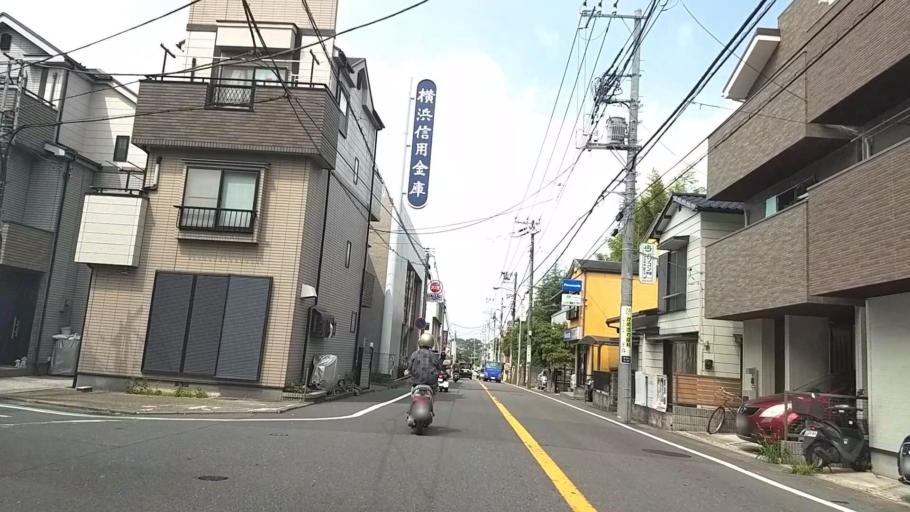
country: JP
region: Kanagawa
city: Yokohama
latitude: 35.4167
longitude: 139.5700
